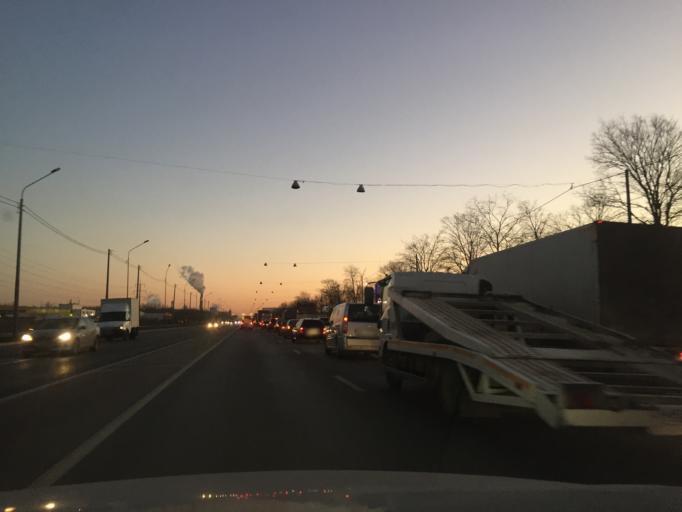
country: RU
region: St.-Petersburg
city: Obukhovo
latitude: 59.8568
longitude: 30.4225
